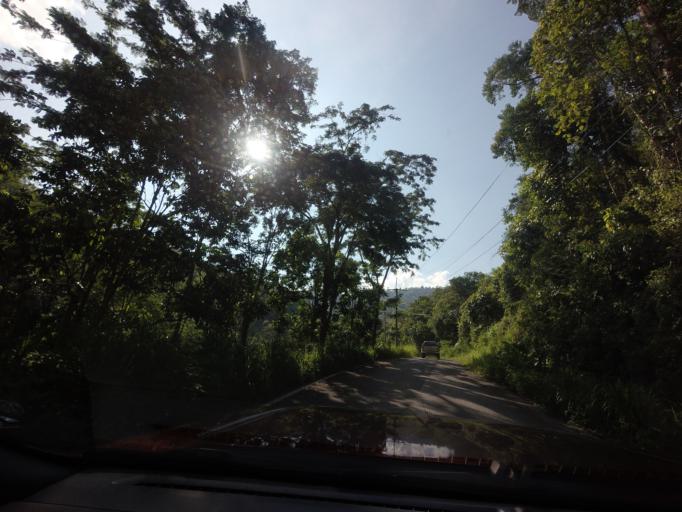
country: TH
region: Yala
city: Than To
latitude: 6.0655
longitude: 101.3588
